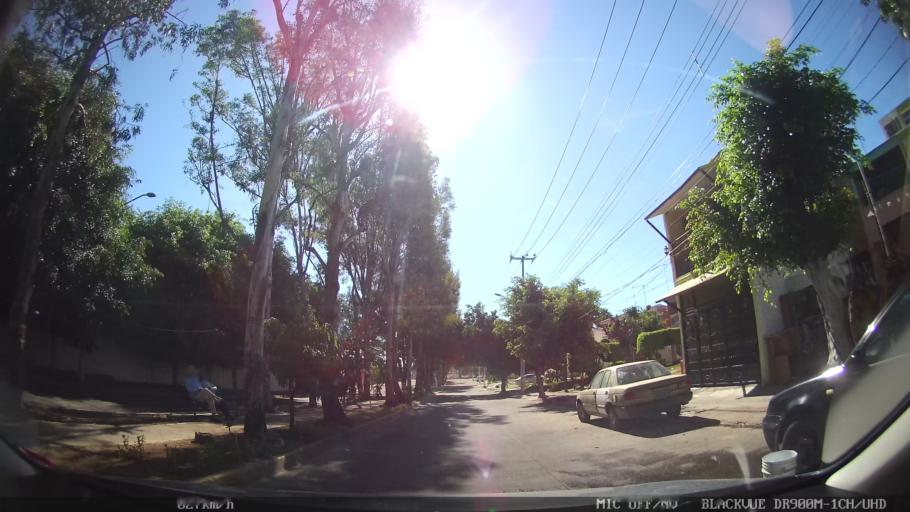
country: MX
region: Jalisco
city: Tlaquepaque
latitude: 20.6829
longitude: -103.2712
